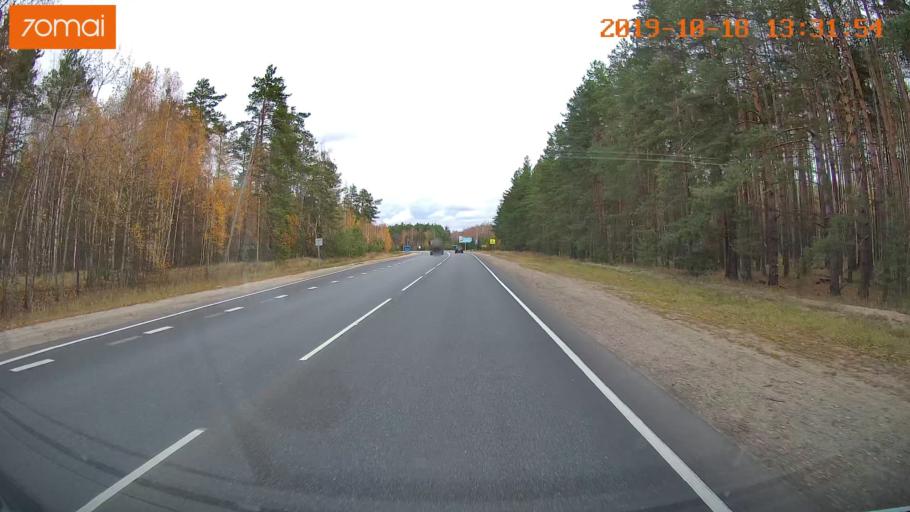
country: RU
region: Rjazan
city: Solotcha
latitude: 54.8266
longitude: 39.9099
